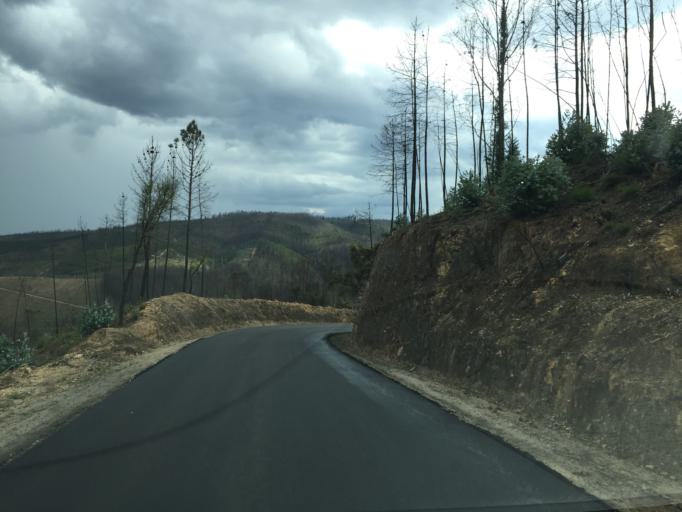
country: PT
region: Coimbra
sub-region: Pampilhosa da Serra
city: Pampilhosa da Serra
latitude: 40.0564
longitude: -8.0168
